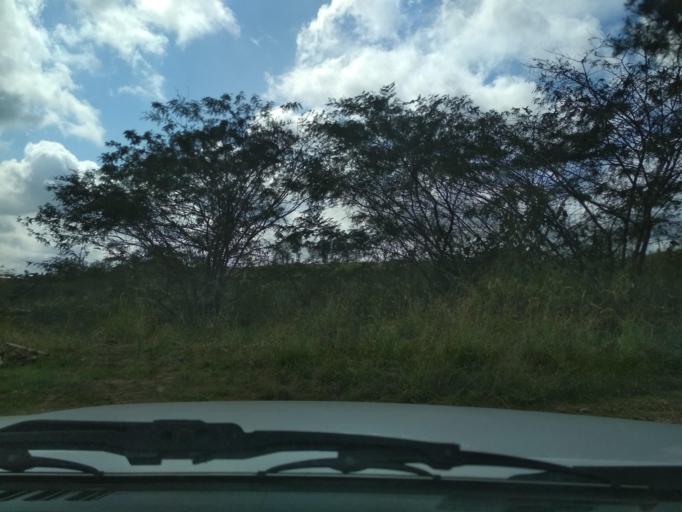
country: MX
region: Veracruz
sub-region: Emiliano Zapata
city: Dos Rios
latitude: 19.5013
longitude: -96.8206
